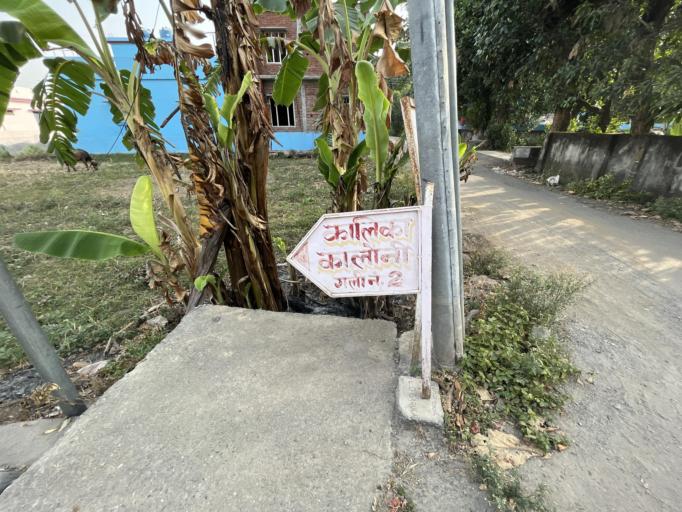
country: IN
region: Uttarakhand
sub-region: Naini Tal
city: Haldwani
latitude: 29.2308
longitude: 79.4811
